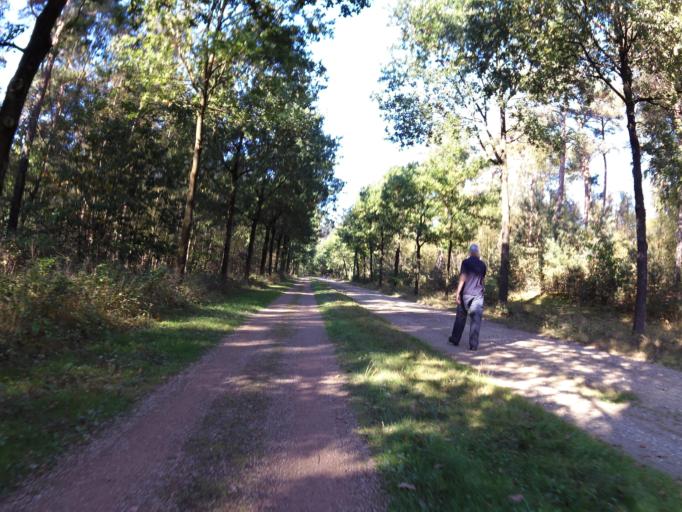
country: NL
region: Limburg
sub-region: Gemeente Venlo
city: Arcen
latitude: 51.4635
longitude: 6.1911
